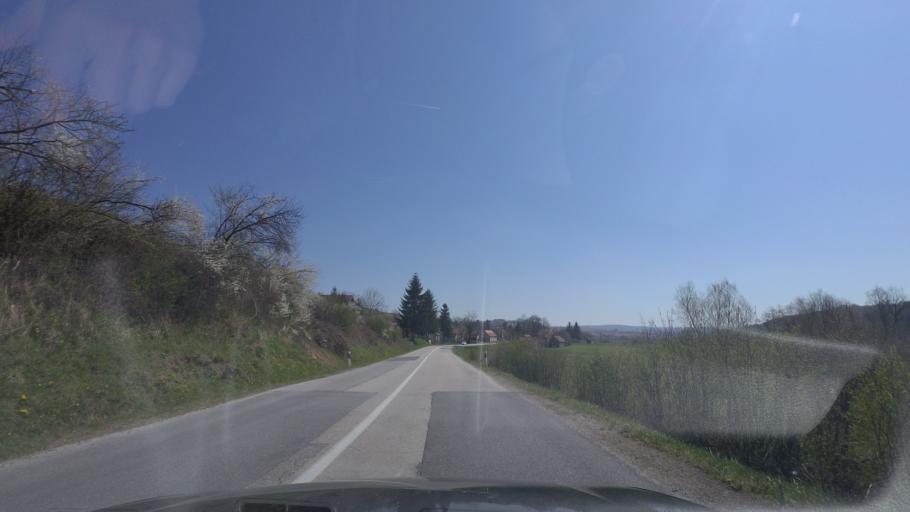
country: HR
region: Karlovacka
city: Vojnic
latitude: 45.3490
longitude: 15.6773
